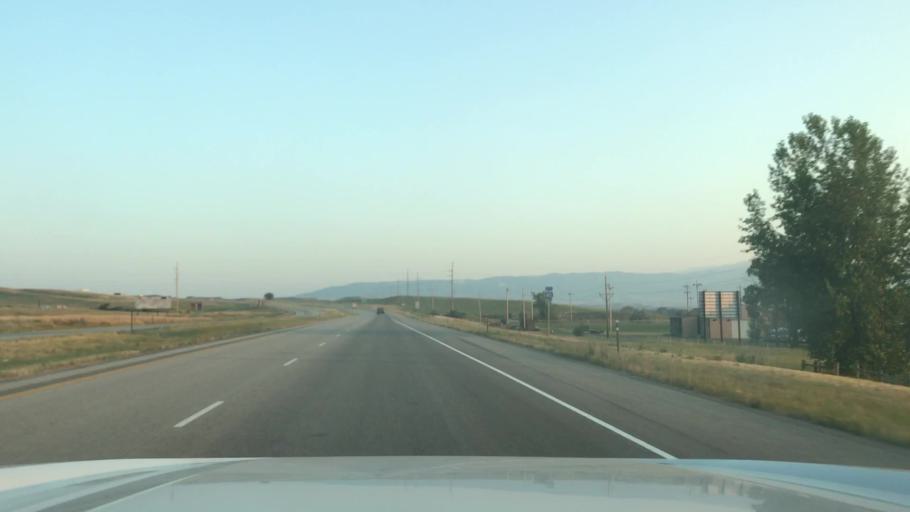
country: US
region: Wyoming
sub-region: Sheridan County
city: Sheridan
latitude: 44.7658
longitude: -106.9370
